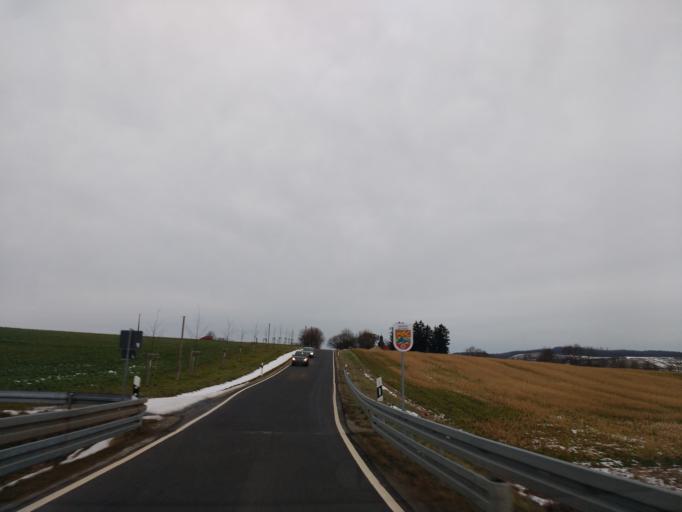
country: DE
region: Thuringia
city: Hohengandern
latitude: 51.3799
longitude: 9.9442
